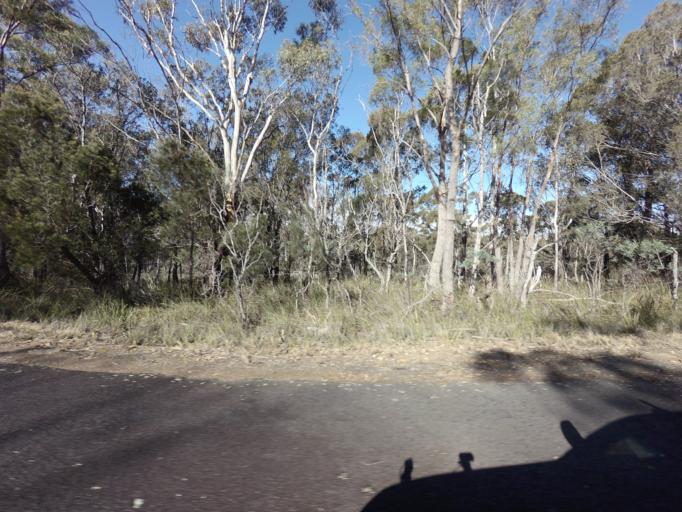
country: AU
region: Tasmania
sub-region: Sorell
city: Sorell
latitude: -42.3600
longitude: 147.9572
